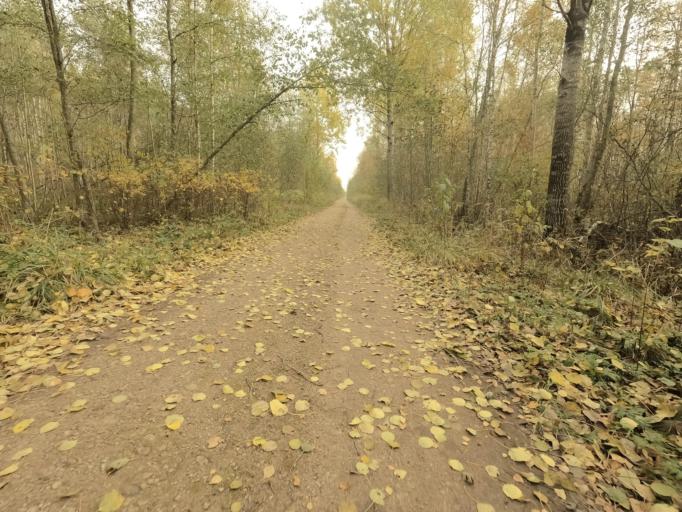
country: RU
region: Novgorod
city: Batetskiy
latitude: 58.8795
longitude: 30.7839
